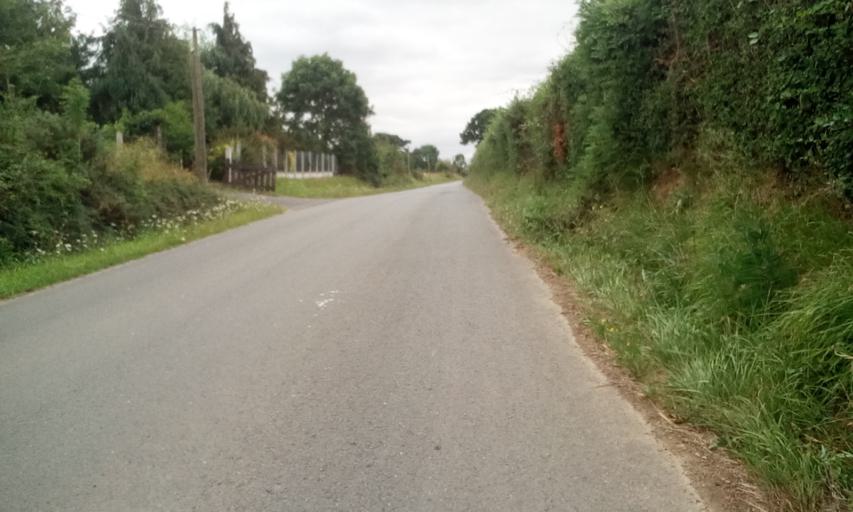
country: FR
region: Lower Normandy
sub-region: Departement du Calvados
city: Troarn
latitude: 49.1960
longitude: -0.1783
